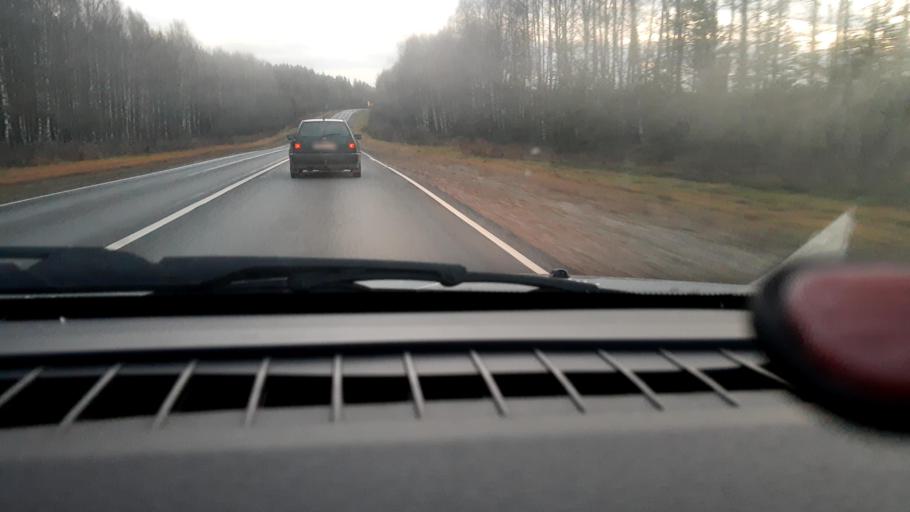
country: RU
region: Nizjnij Novgorod
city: Krasnyye Baki
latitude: 57.0361
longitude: 45.1238
